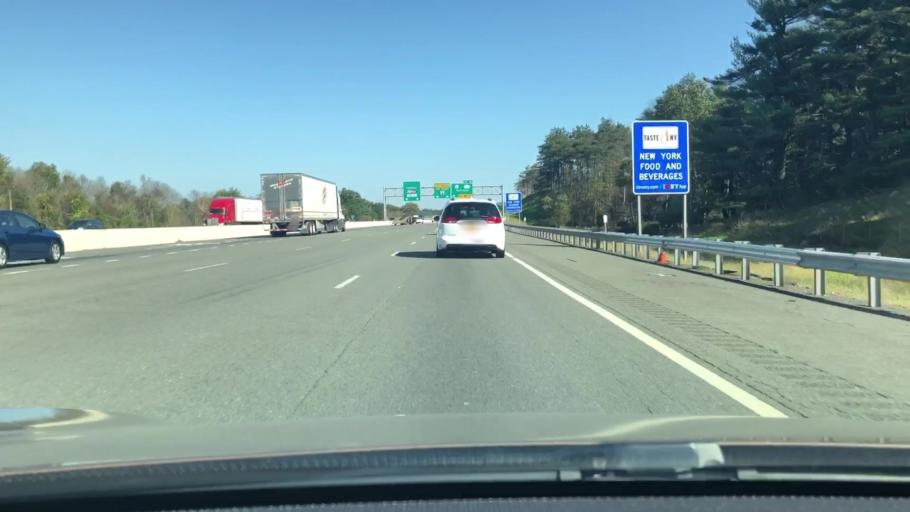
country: US
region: New York
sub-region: Orange County
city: Harriman
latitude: 41.3004
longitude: -74.1345
